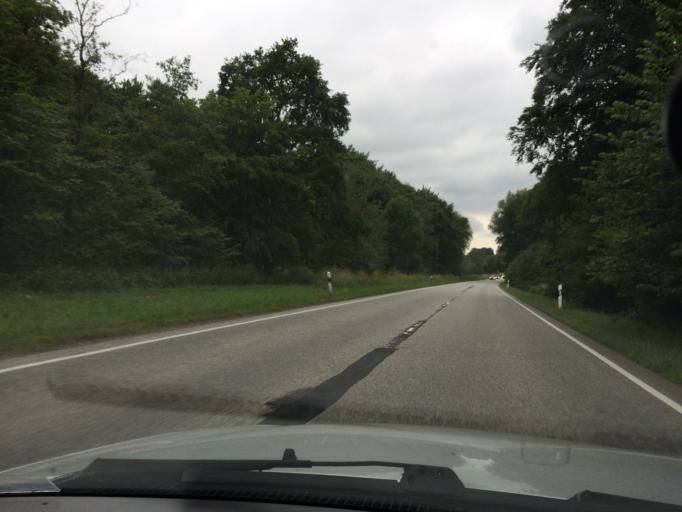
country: DE
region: Schleswig-Holstein
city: Oeversee
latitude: 54.6754
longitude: 9.4385
